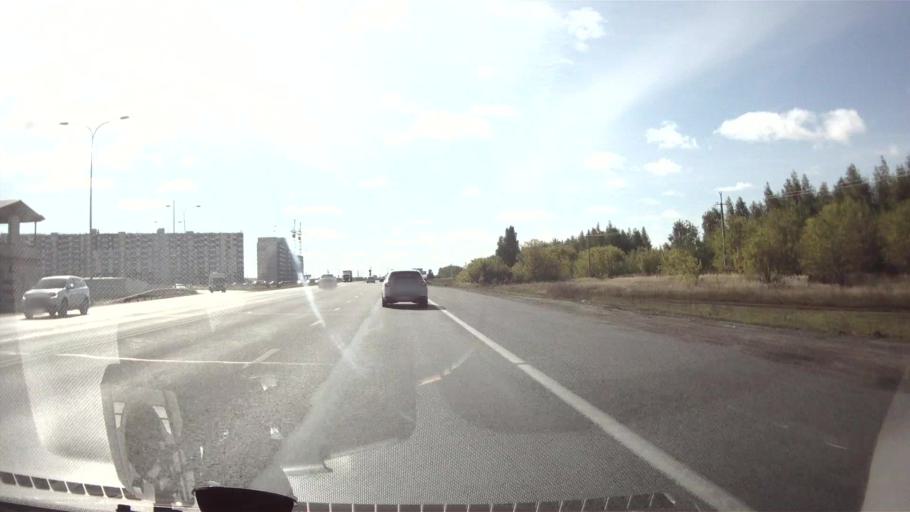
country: RU
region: Ulyanovsk
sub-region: Ulyanovskiy Rayon
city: Ulyanovsk
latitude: 54.2865
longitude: 48.2565
